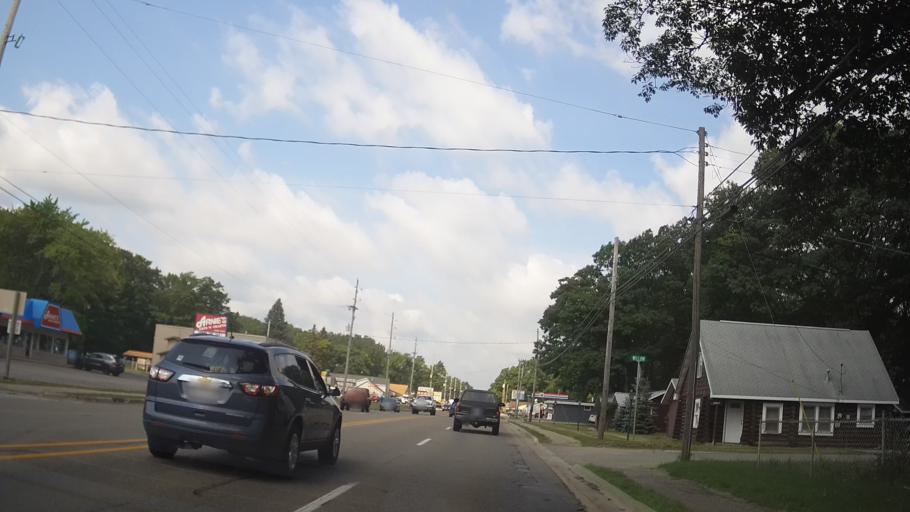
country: US
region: Michigan
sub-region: Roscommon County
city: Houghton Lake
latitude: 44.2986
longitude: -84.7138
